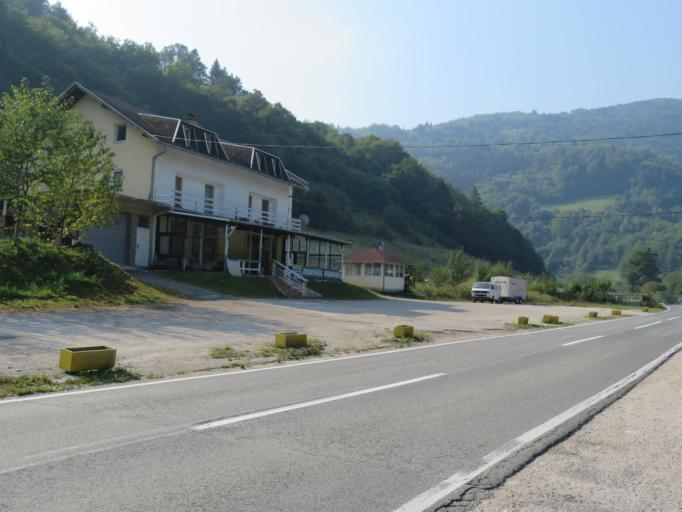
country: BA
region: Federation of Bosnia and Herzegovina
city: Jajce
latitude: 44.2343
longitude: 17.3042
